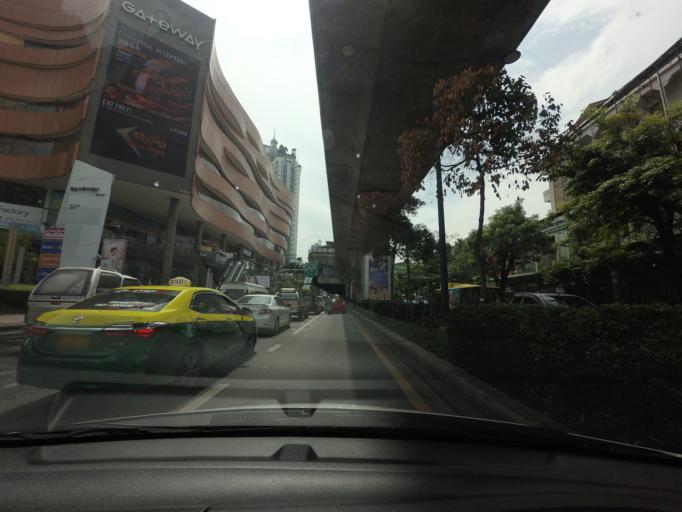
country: TH
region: Bangkok
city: Watthana
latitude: 13.7187
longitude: 100.5862
